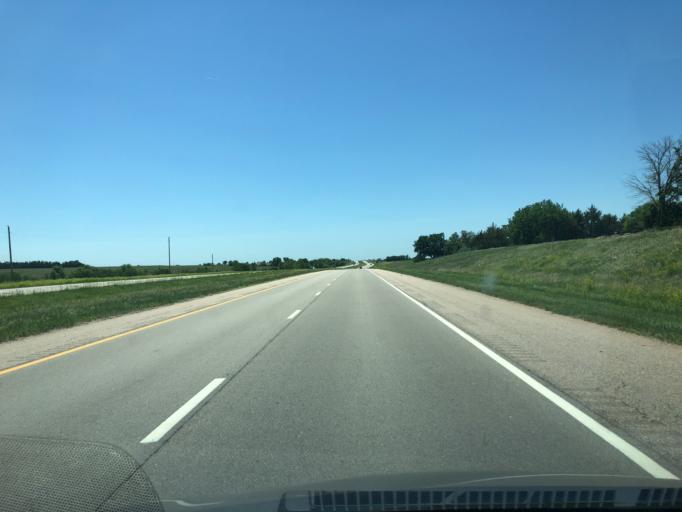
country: US
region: Kansas
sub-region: Republic County
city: Belleville
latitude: 39.9539
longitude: -97.6137
